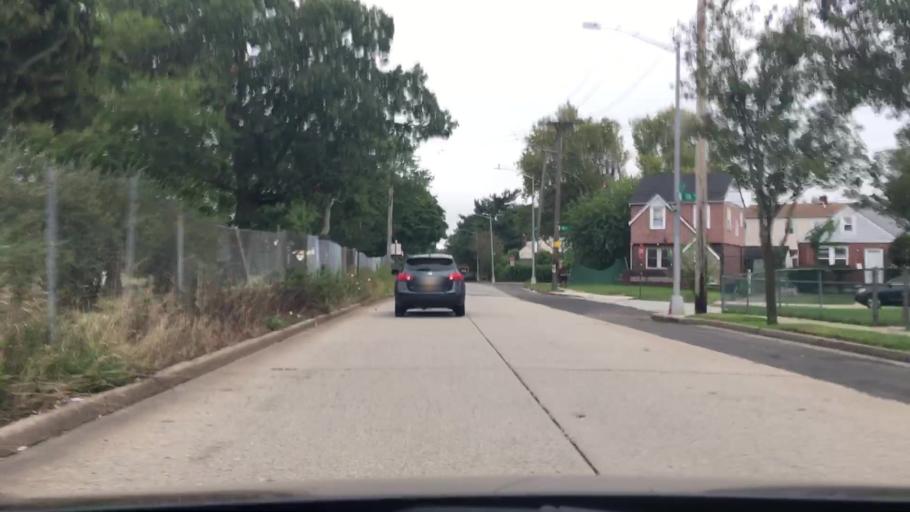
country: US
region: New York
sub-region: Nassau County
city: Elmont
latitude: 40.6898
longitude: -73.7271
